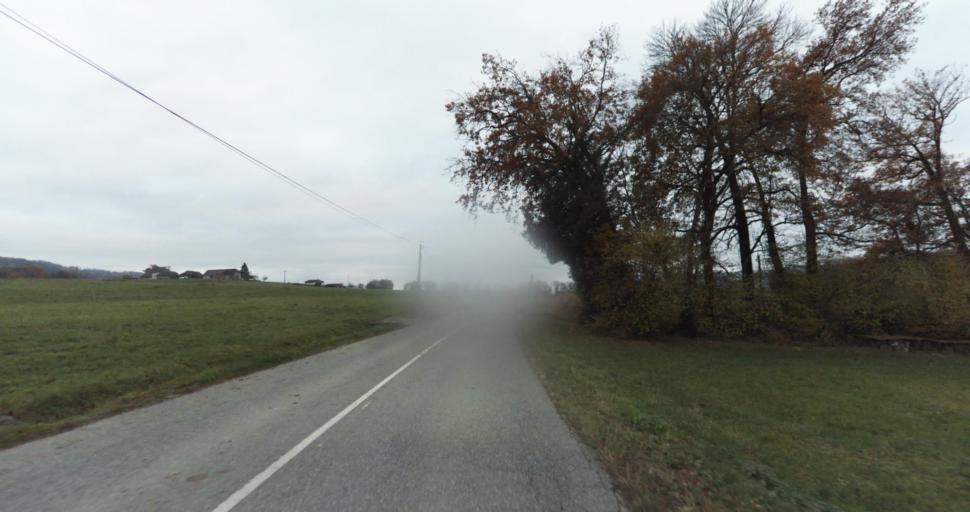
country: FR
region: Rhone-Alpes
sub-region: Departement de la Haute-Savoie
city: Saint-Felix
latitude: 45.8184
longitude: 5.9746
